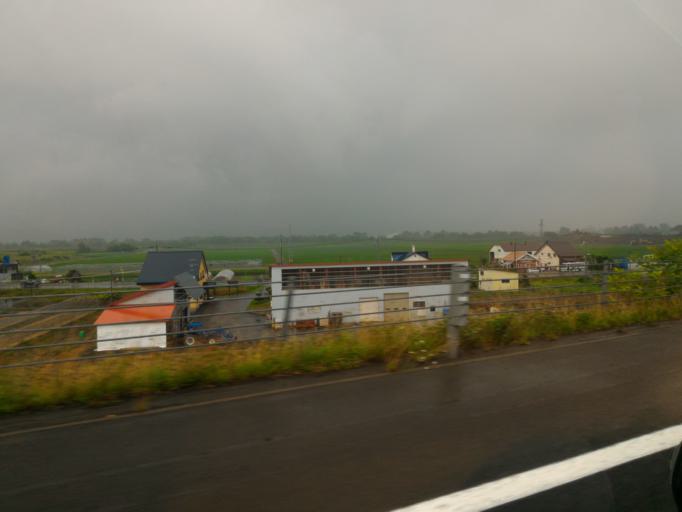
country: JP
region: Hokkaido
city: Nayoro
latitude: 44.3703
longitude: 142.4344
